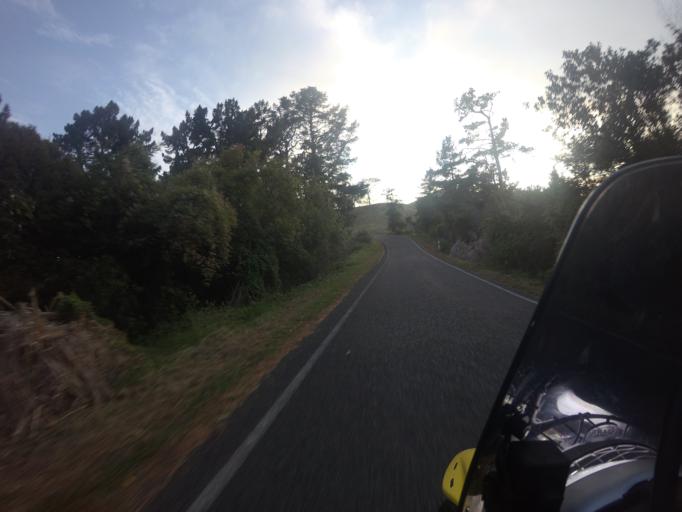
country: NZ
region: Gisborne
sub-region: Gisborne District
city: Gisborne
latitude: -38.6646
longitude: 178.0571
